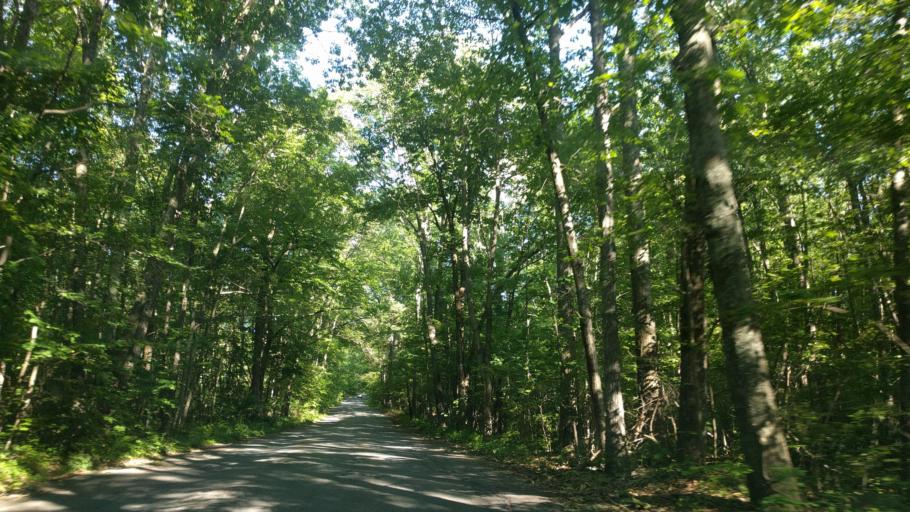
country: US
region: Massachusetts
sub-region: Worcester County
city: Oxford
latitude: 42.1479
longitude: -71.8508
